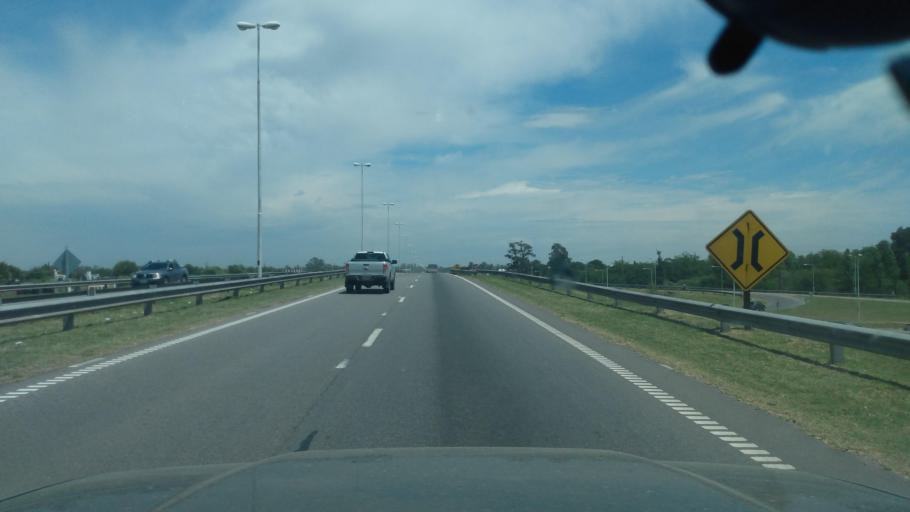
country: AR
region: Buenos Aires
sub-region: Partido de Lujan
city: Lujan
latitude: -34.5567
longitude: -59.0988
